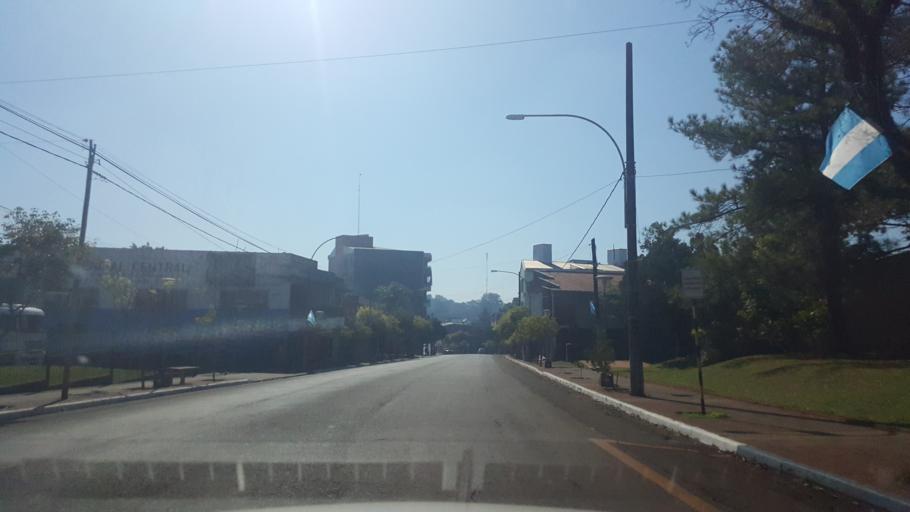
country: AR
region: Misiones
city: Puerto Rico
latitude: -26.8166
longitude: -55.0272
